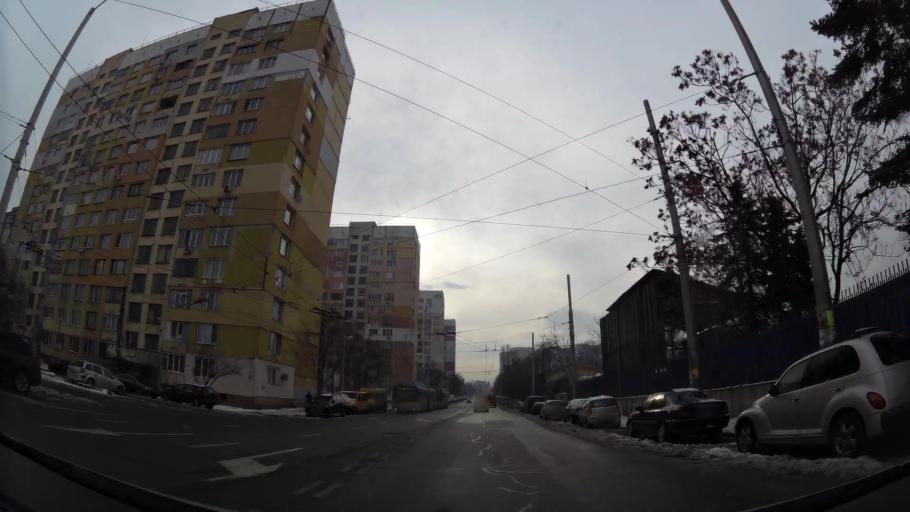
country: BG
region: Sofia-Capital
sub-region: Stolichna Obshtina
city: Sofia
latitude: 42.7133
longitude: 23.3078
